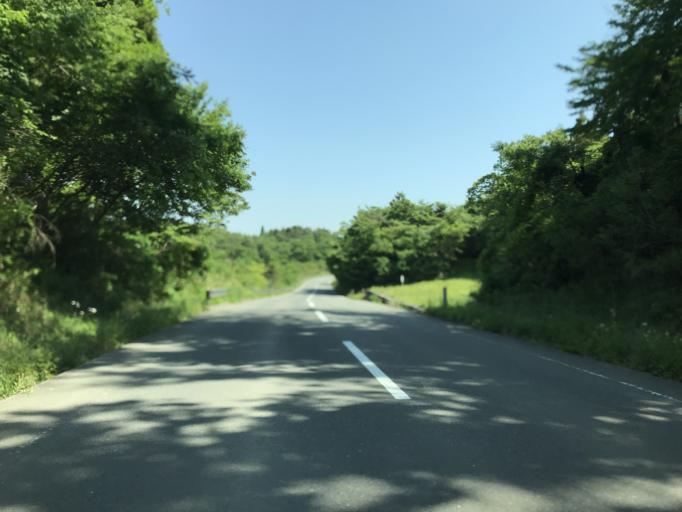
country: JP
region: Miyagi
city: Marumori
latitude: 37.8197
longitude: 140.8798
